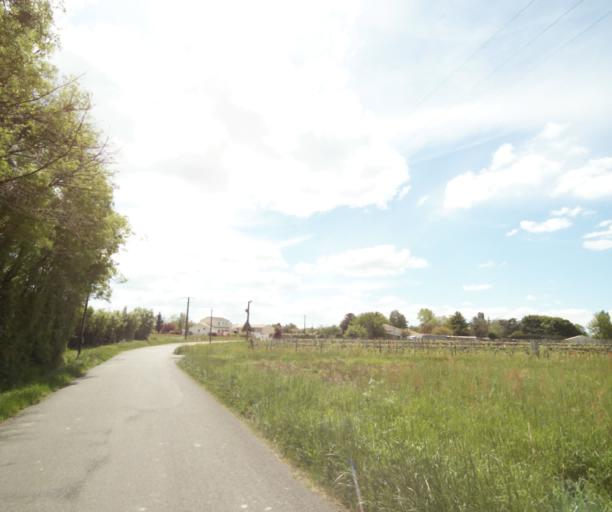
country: FR
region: Poitou-Charentes
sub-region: Departement de la Charente-Maritime
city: Burie
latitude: 45.7500
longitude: -0.4462
